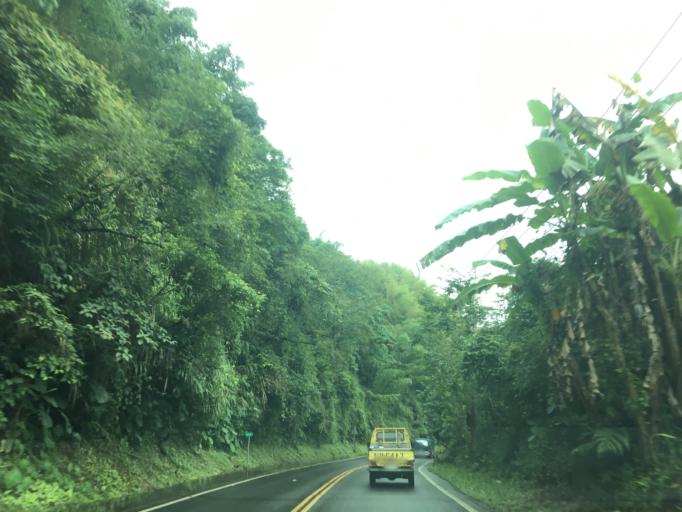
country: TW
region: Taiwan
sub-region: Chiayi
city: Jiayi Shi
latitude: 23.4406
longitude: 120.6703
